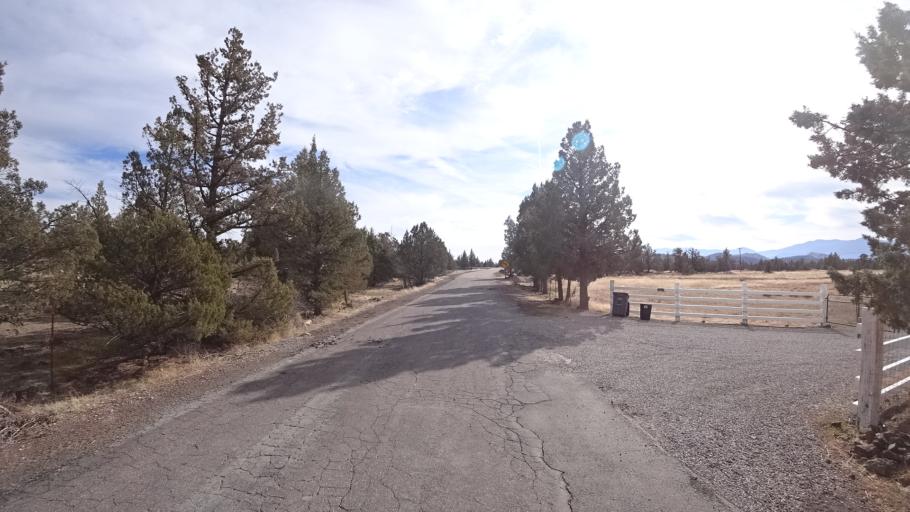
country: US
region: California
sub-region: Siskiyou County
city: Weed
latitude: 41.5926
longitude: -122.4011
